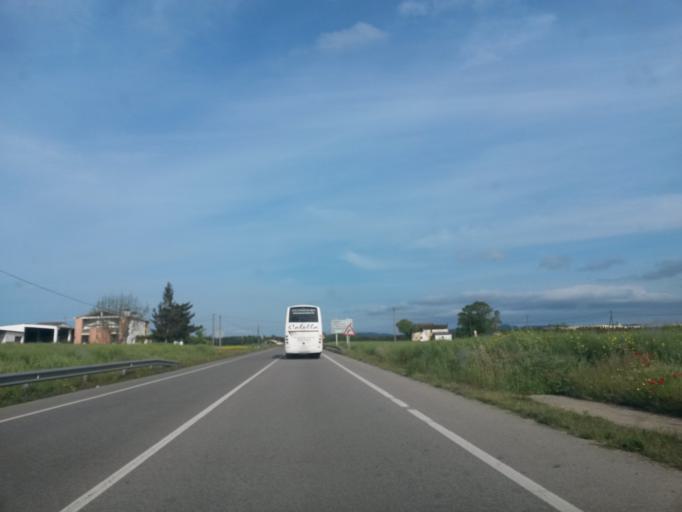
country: ES
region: Catalonia
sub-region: Provincia de Girona
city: Sils
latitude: 41.8034
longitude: 2.7672
